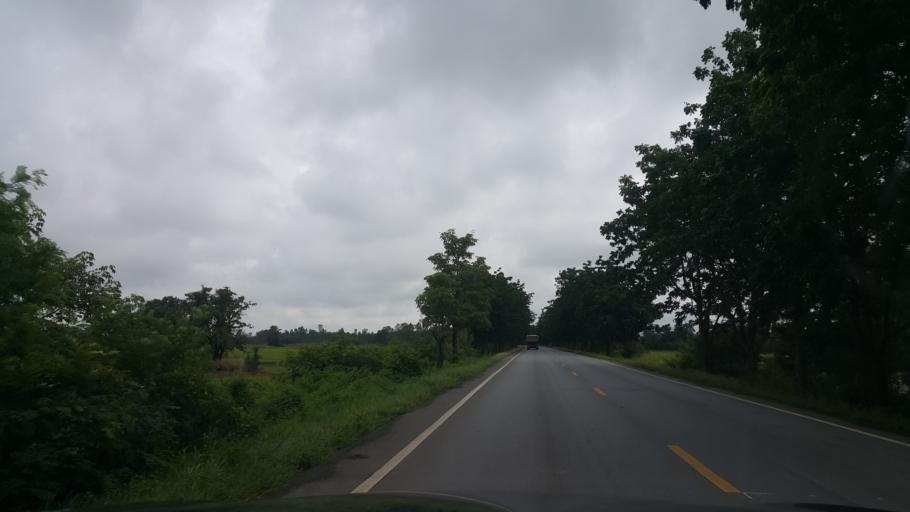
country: TH
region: Sukhothai
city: Sawankhalok
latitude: 17.3374
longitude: 99.7418
